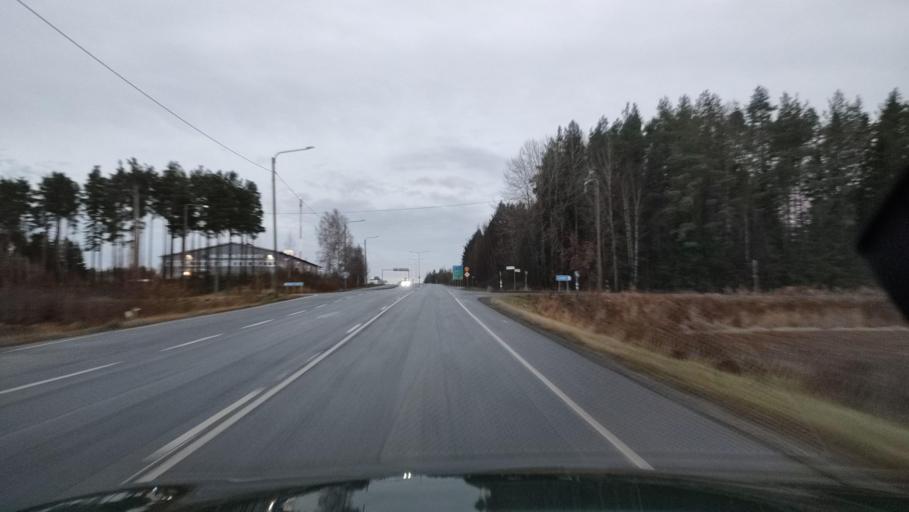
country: FI
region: Ostrobothnia
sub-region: Vaasa
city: Ristinummi
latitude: 63.0317
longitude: 21.7577
